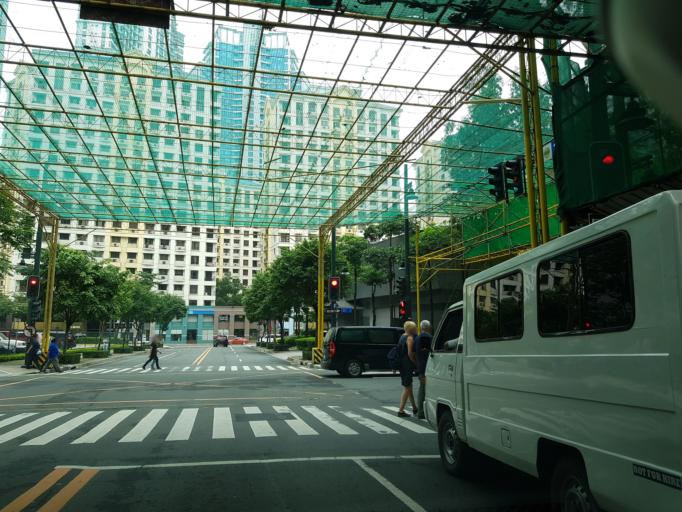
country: PH
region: Metro Manila
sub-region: Makati City
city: Makati City
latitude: 14.5513
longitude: 121.0462
